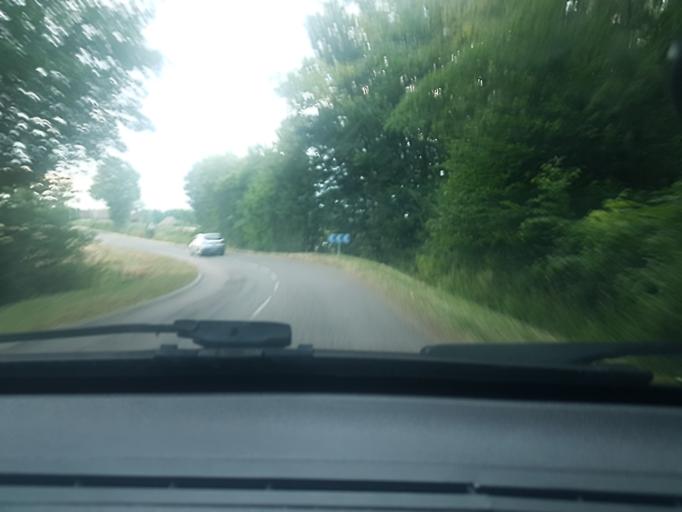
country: FR
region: Bourgogne
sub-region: Departement de Saone-et-Loire
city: Sevrey
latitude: 46.6994
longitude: 4.7775
